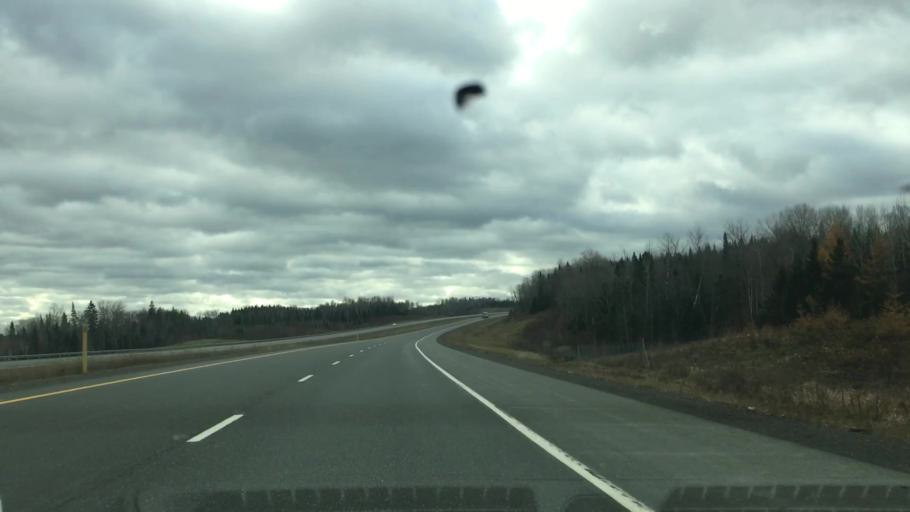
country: US
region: Maine
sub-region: Aroostook County
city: Fort Fairfield
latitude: 46.6693
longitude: -67.7296
